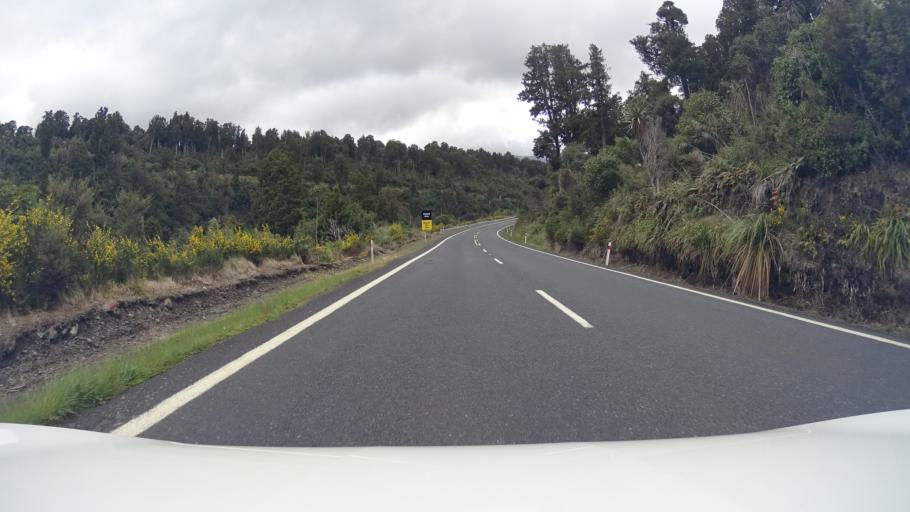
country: NZ
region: Manawatu-Wanganui
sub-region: Ruapehu District
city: Waiouru
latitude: -39.2660
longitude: 175.3923
